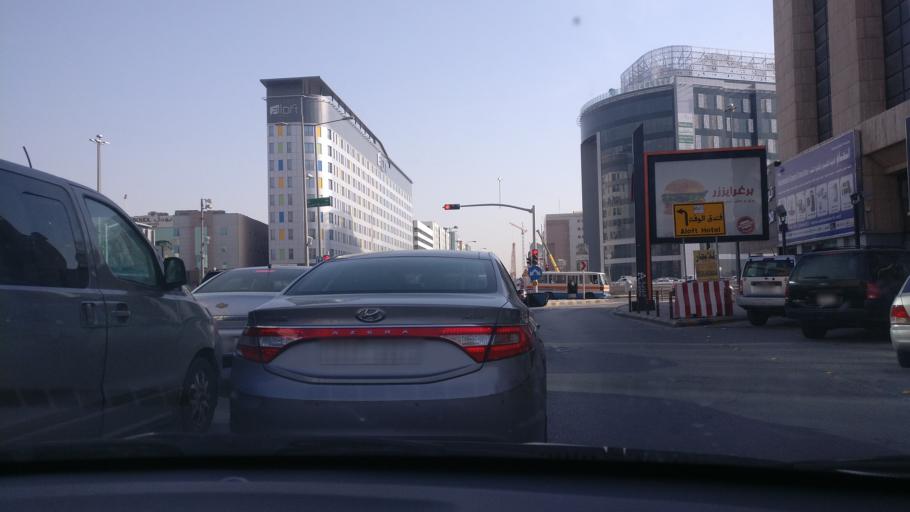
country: SA
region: Ar Riyad
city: Riyadh
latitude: 24.6809
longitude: 46.6915
